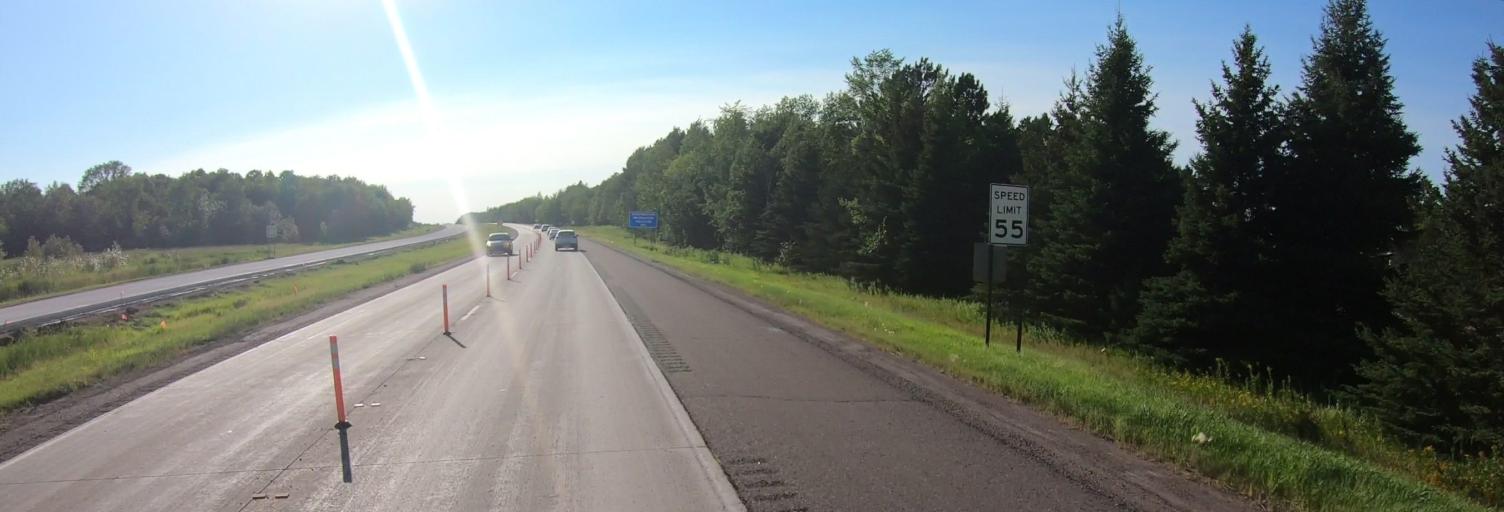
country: US
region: Minnesota
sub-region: Saint Louis County
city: Hermantown
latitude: 46.8518
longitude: -92.2892
